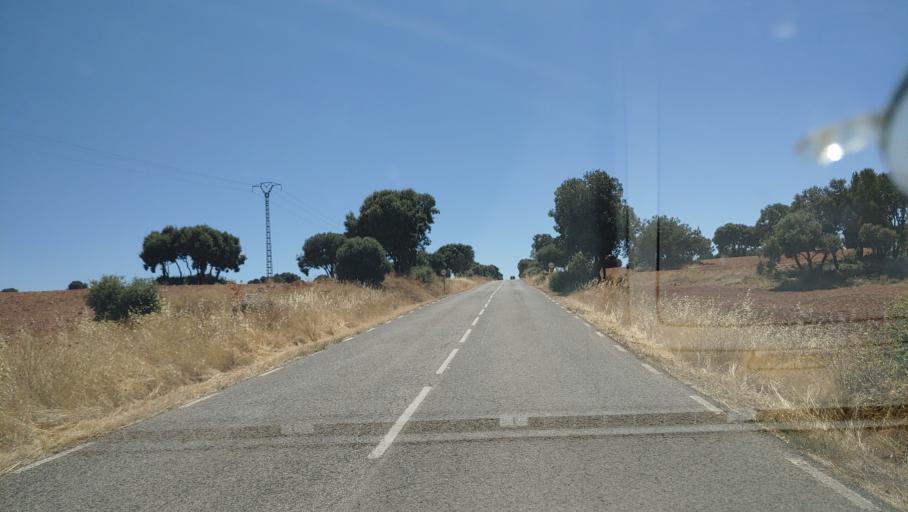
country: ES
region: Castille-La Mancha
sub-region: Provincia de Albacete
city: Ossa de Montiel
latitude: 38.9291
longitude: -2.7534
